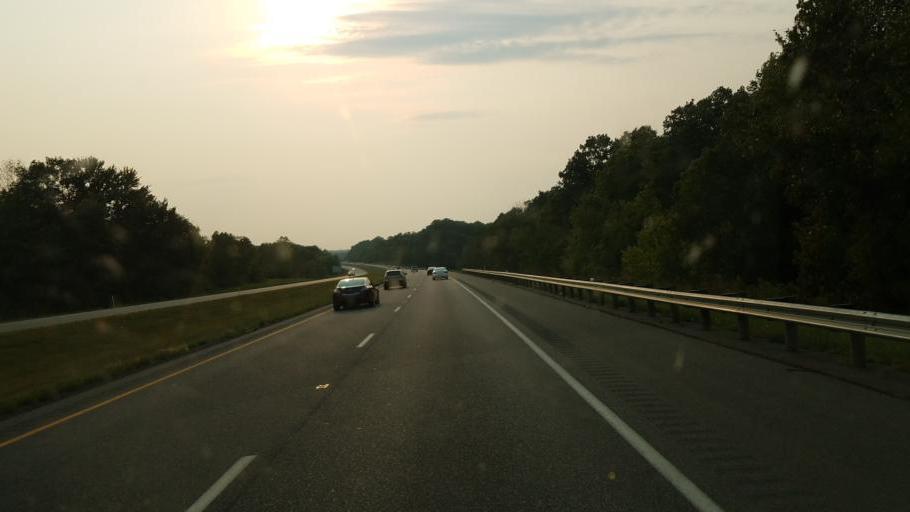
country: US
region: Ohio
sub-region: Geauga County
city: Bainbridge
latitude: 41.3898
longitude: -81.3571
